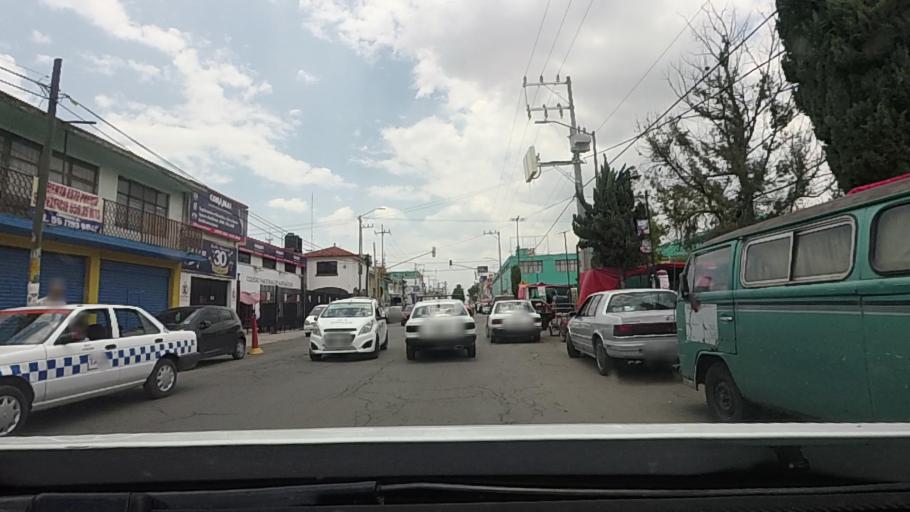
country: MX
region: Mexico
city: Chalco de Diaz Covarrubias
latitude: 19.2597
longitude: -98.8944
